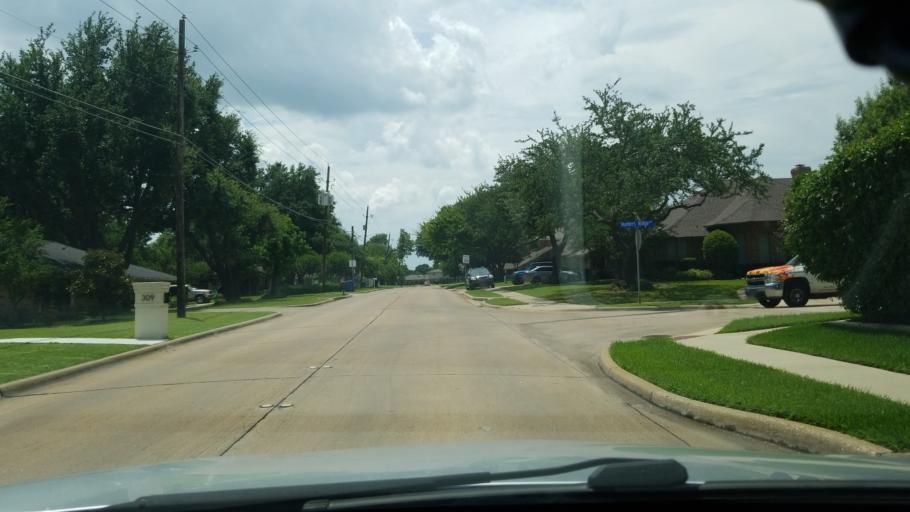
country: US
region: Texas
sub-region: Dallas County
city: Coppell
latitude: 32.9600
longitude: -96.9866
